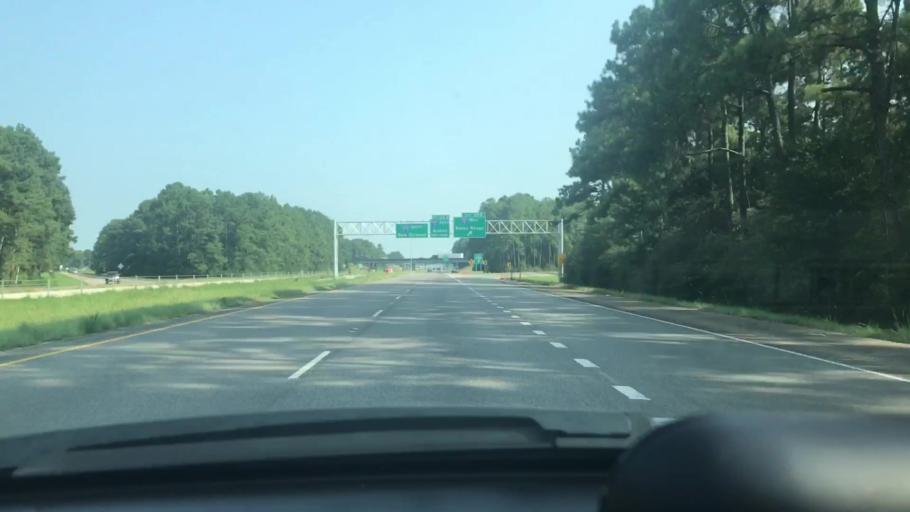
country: US
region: Louisiana
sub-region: Tangipahoa Parish
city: Hammond
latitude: 30.4828
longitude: -90.4921
